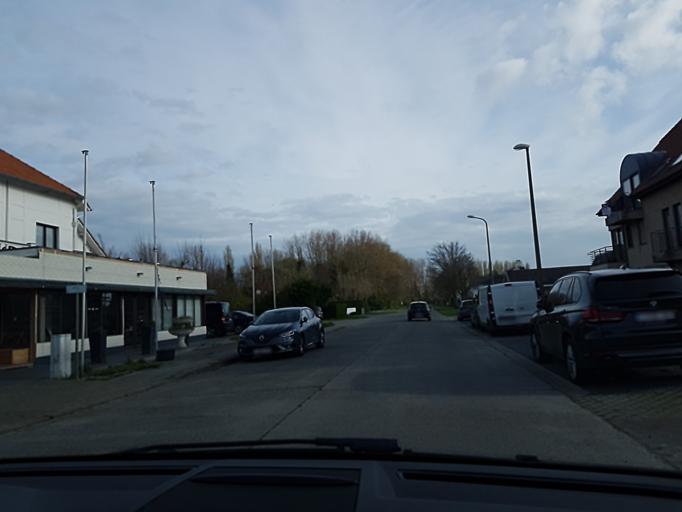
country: BE
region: Flanders
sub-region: Provincie West-Vlaanderen
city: Bredene
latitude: 51.2519
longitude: 2.9868
